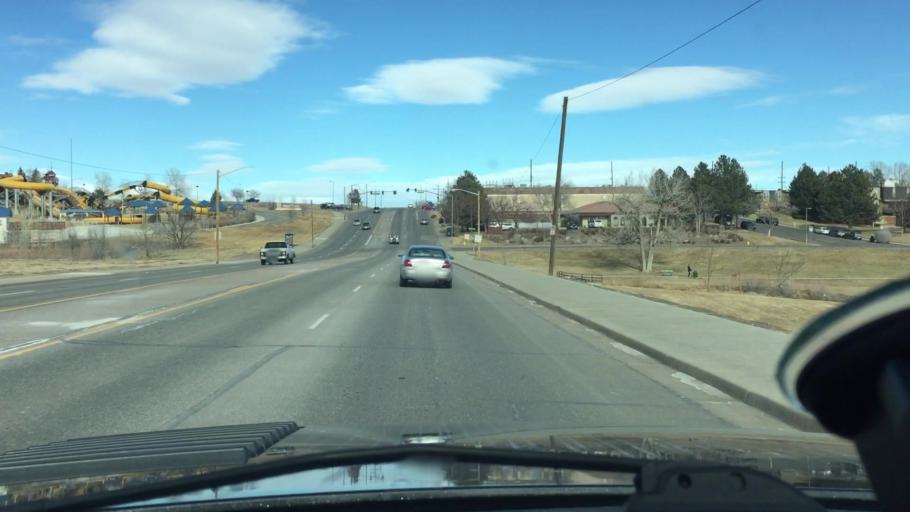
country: US
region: Colorado
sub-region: Adams County
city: Federal Heights
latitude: 39.8535
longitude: -105.0060
